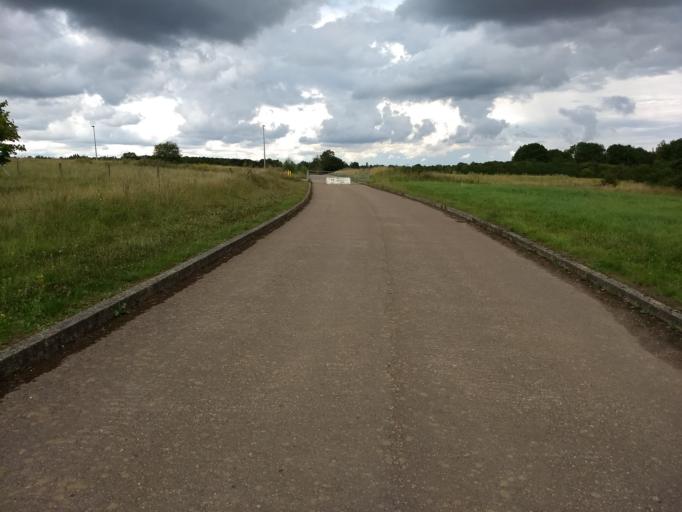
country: GB
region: England
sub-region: Buckinghamshire
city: Newton Longville
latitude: 51.9898
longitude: -0.7982
